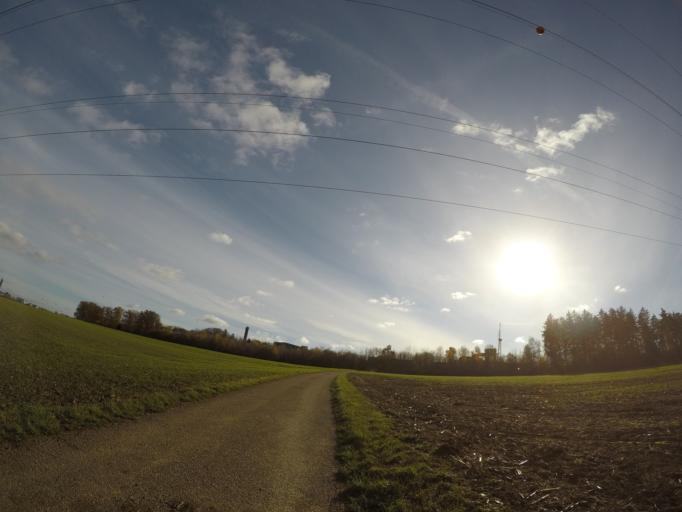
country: DE
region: Baden-Wuerttemberg
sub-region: Tuebingen Region
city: Dornstadt
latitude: 48.4292
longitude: 9.9466
